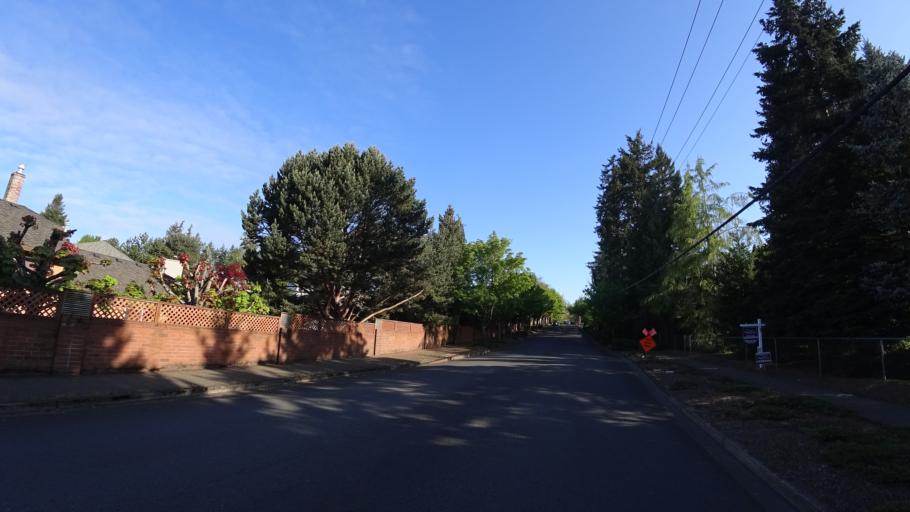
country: US
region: Oregon
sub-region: Washington County
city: Beaverton
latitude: 45.4463
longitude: -122.8208
